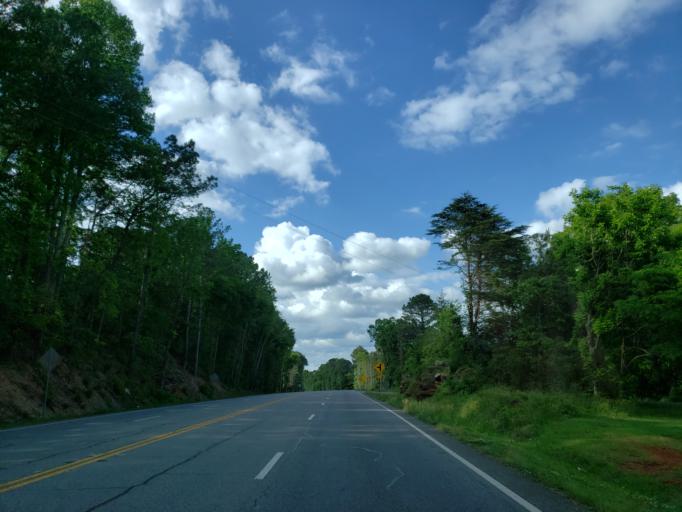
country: US
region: Georgia
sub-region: Bartow County
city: Cartersville
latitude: 34.2482
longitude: -84.8573
